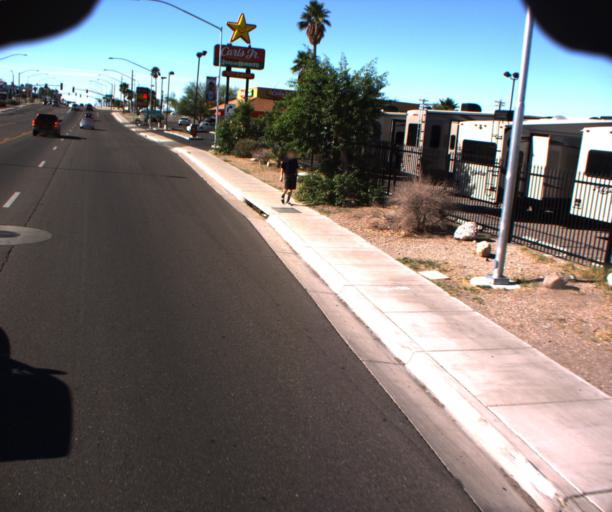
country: US
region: Arizona
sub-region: Mohave County
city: Bullhead City
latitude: 35.1094
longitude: -114.5981
